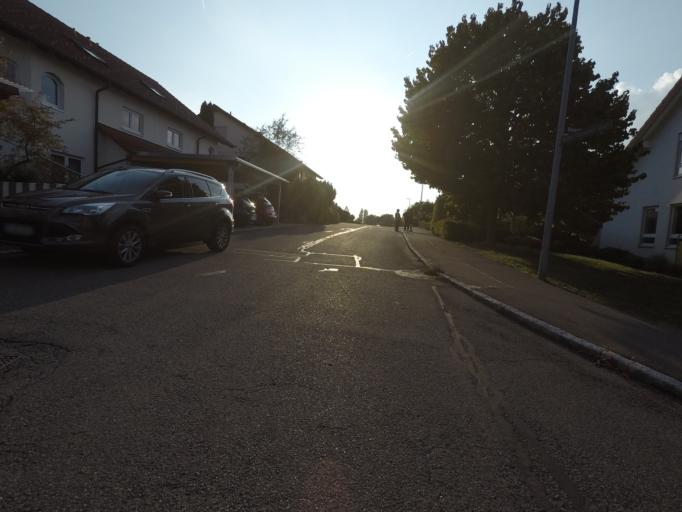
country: DE
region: Baden-Wuerttemberg
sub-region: Tuebingen Region
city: Pfullingen
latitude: 48.4638
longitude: 9.2370
